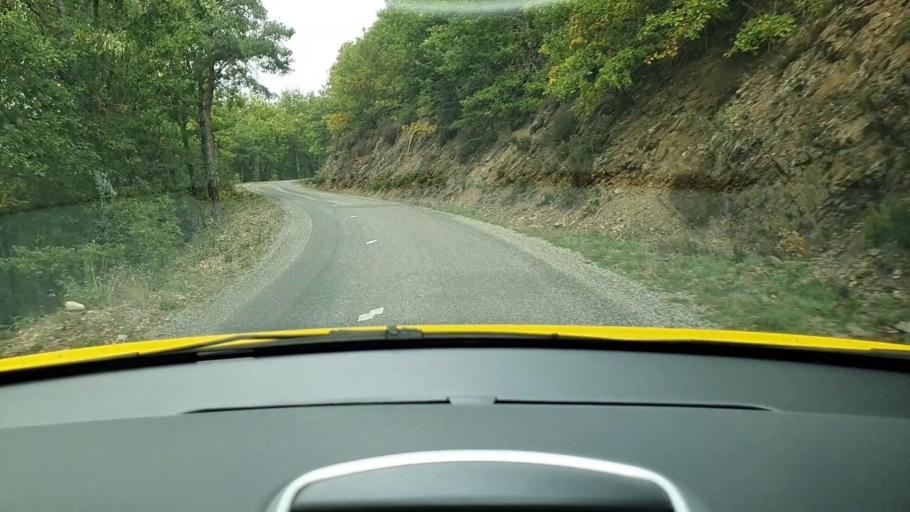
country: FR
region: Languedoc-Roussillon
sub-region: Departement de la Lozere
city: Meyrueis
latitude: 44.0700
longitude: 3.4082
